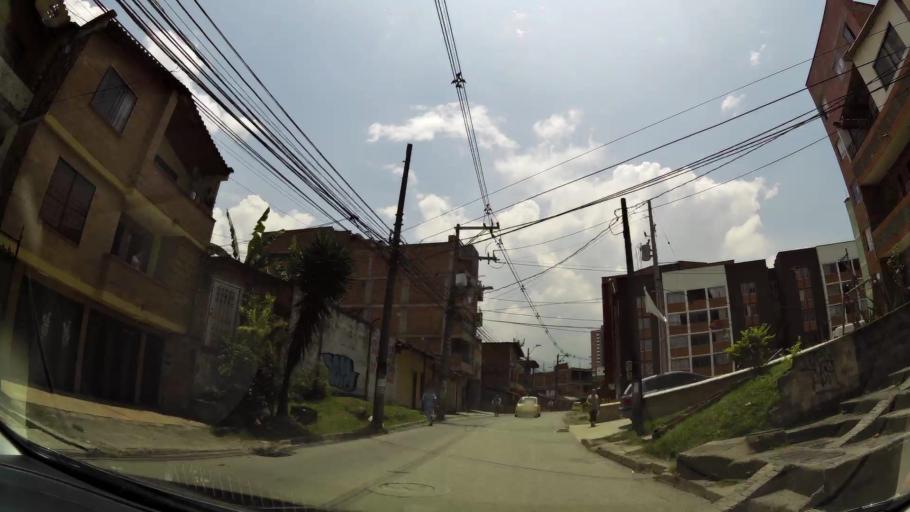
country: CO
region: Antioquia
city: Sabaneta
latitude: 6.1713
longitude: -75.6170
